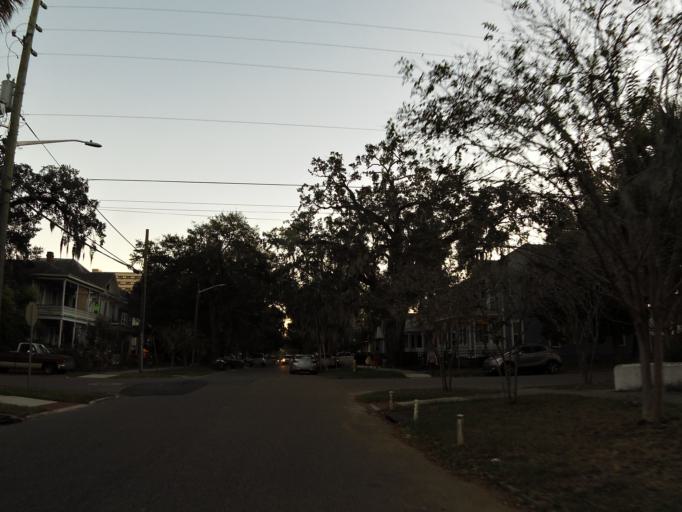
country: US
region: Florida
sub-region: Duval County
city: Jacksonville
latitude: 30.3378
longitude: -81.6517
